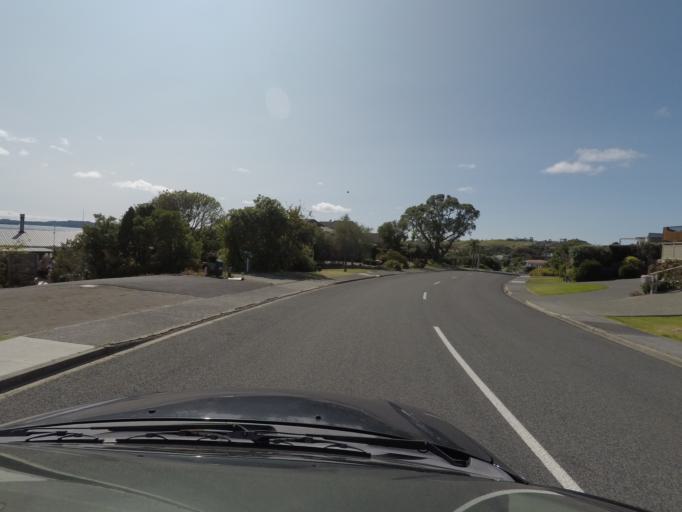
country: NZ
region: Auckland
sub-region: Auckland
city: Warkworth
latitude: -36.4311
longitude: 174.7408
